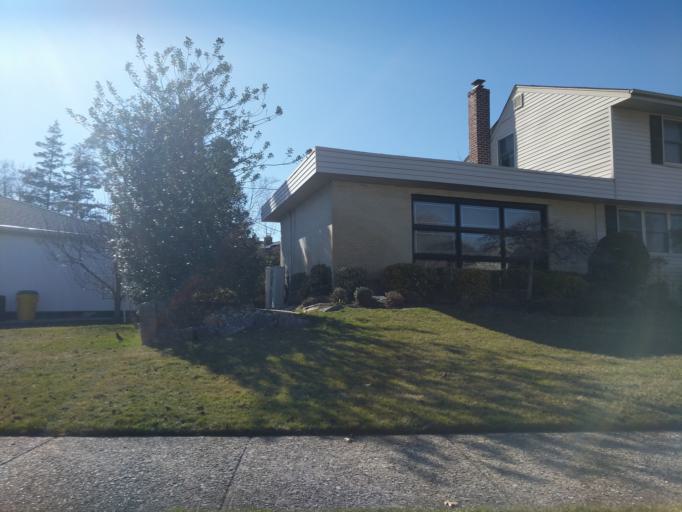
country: US
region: New York
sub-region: Nassau County
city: South Valley Stream
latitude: 40.6485
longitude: -73.7240
